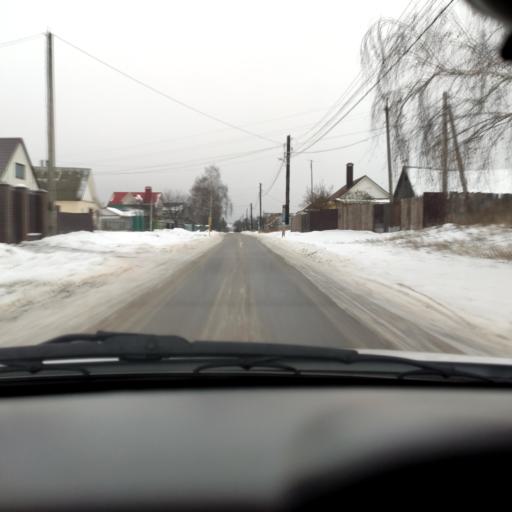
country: RU
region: Voronezj
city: Ramon'
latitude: 51.8883
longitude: 39.2685
